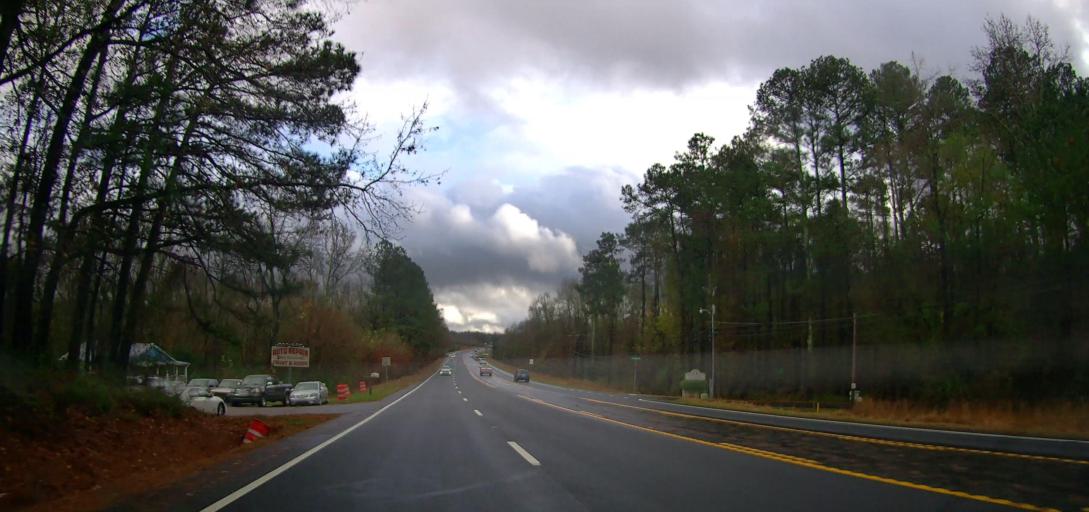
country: US
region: Georgia
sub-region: Clarke County
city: Athens
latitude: 33.9898
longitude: -83.3783
